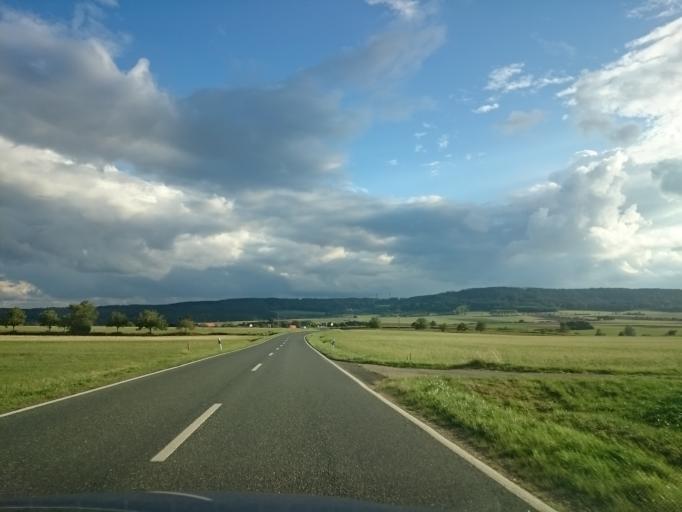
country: DE
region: Bavaria
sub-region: Regierungsbezirk Mittelfranken
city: Thalmassing
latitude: 49.1174
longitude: 11.1823
